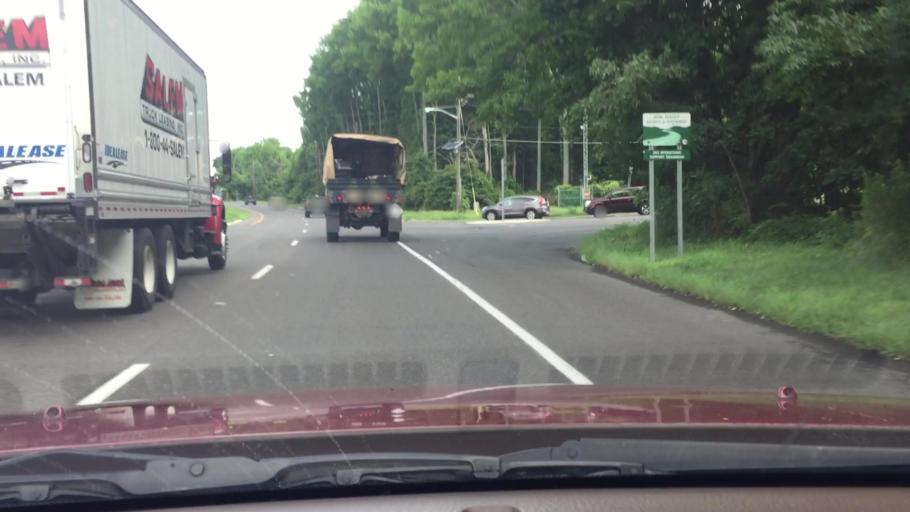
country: US
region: New Jersey
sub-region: Burlington County
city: Fort Dix
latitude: 40.0721
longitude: -74.6565
